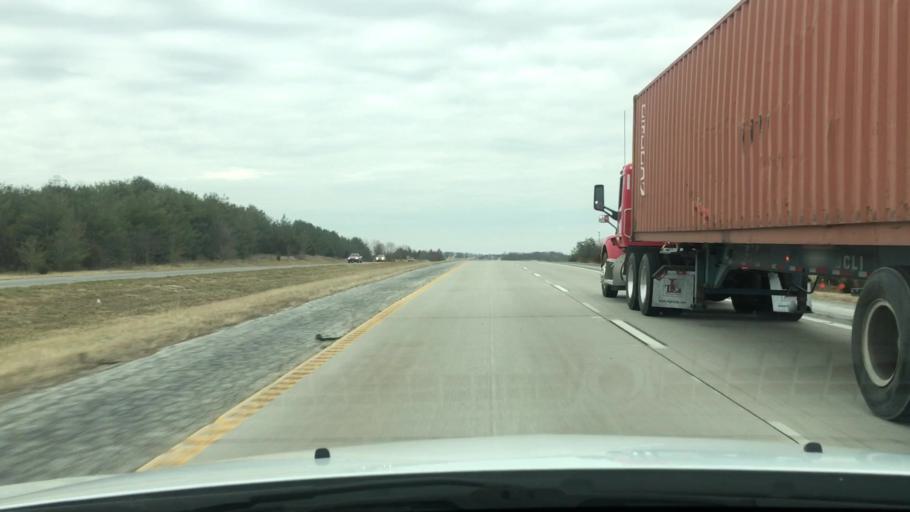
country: US
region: Missouri
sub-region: Audrain County
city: Mexico
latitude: 39.0939
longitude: -91.8990
